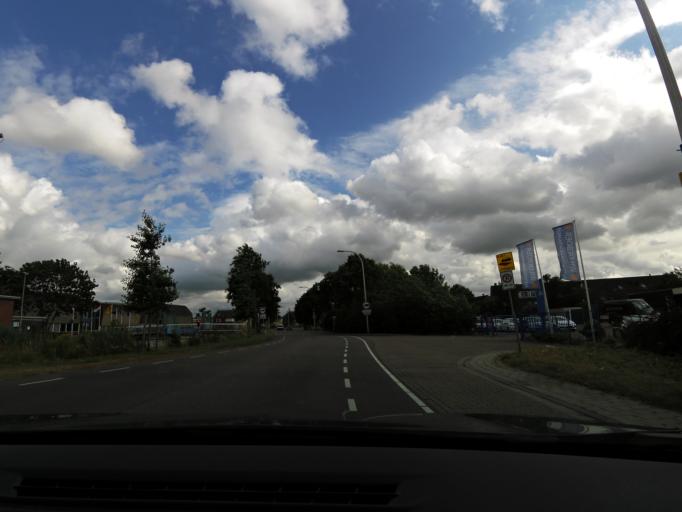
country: NL
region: South Holland
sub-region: Gemeente Delft
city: Delft
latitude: 51.9805
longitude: 4.3168
